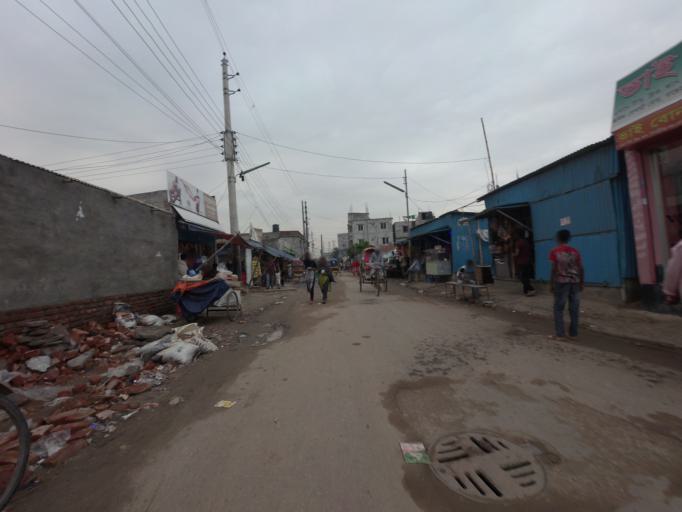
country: BD
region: Dhaka
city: Azimpur
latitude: 23.7773
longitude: 90.3482
